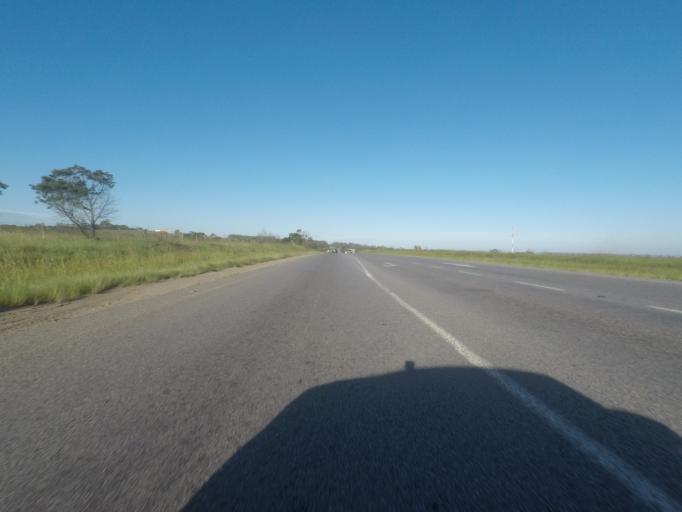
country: ZA
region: Eastern Cape
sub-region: Buffalo City Metropolitan Municipality
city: East London
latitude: -33.0522
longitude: 27.8095
